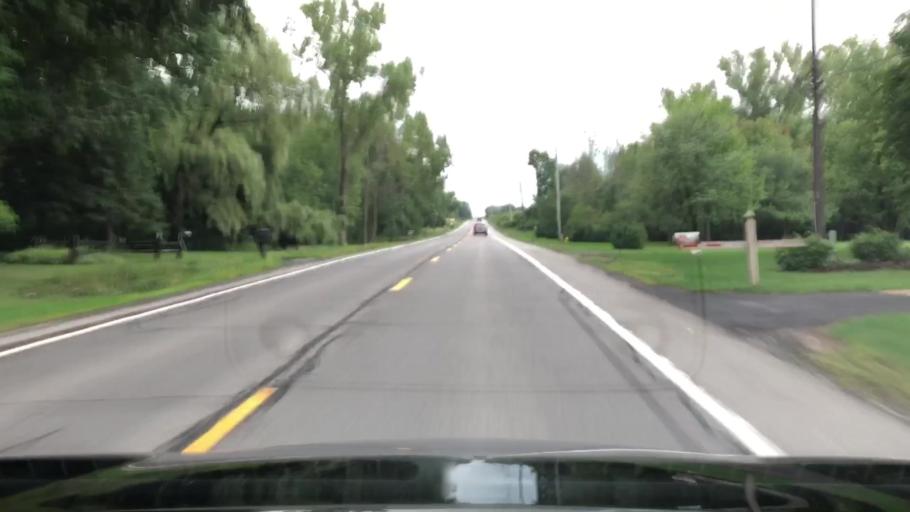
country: US
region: New York
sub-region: Erie County
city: Orchard Park
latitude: 42.7968
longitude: -78.6969
